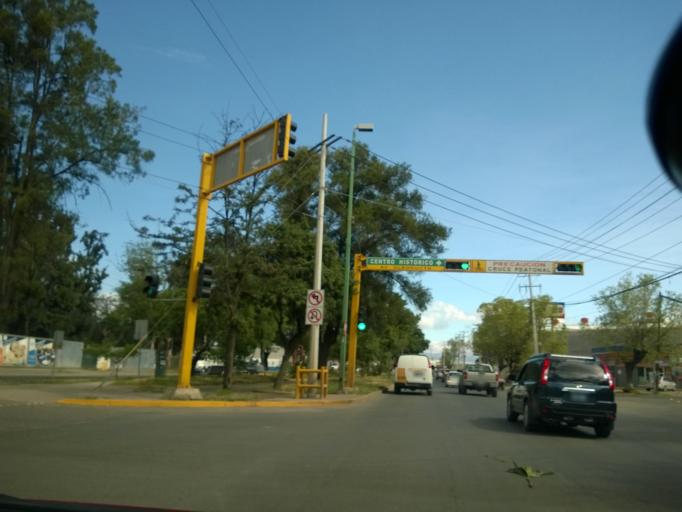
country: MX
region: Guanajuato
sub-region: Leon
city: San Jose de Duran (Los Troncoso)
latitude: 21.0767
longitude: -101.6813
